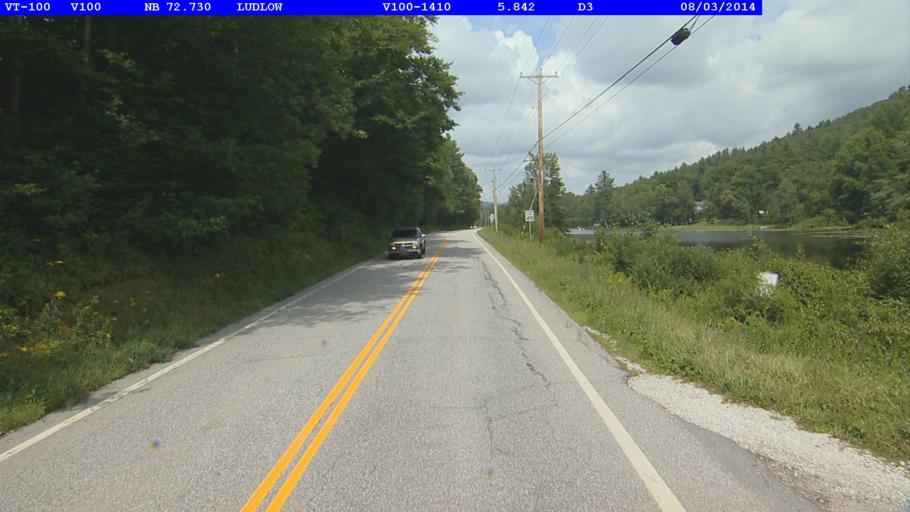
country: US
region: Vermont
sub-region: Windsor County
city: Chester
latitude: 43.4295
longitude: -72.6985
